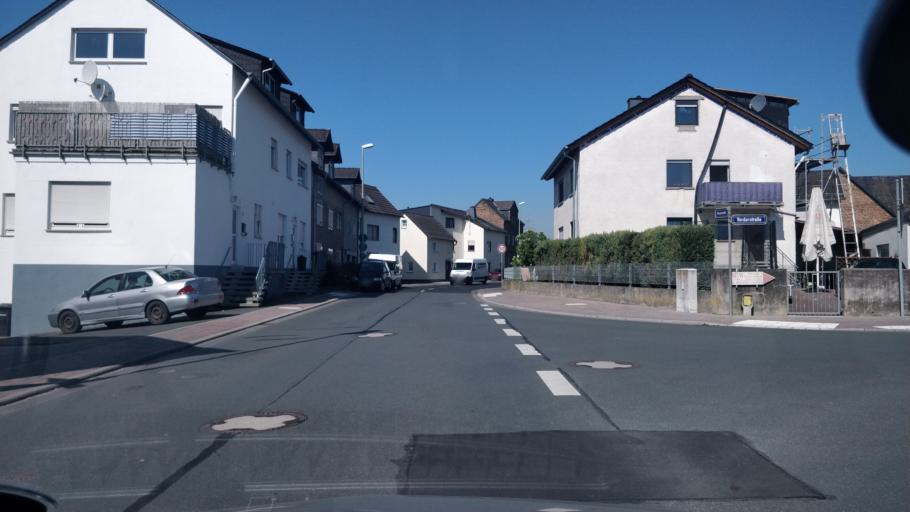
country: DE
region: Hesse
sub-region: Regierungsbezirk Giessen
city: Dehrn
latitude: 50.4368
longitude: 8.0829
